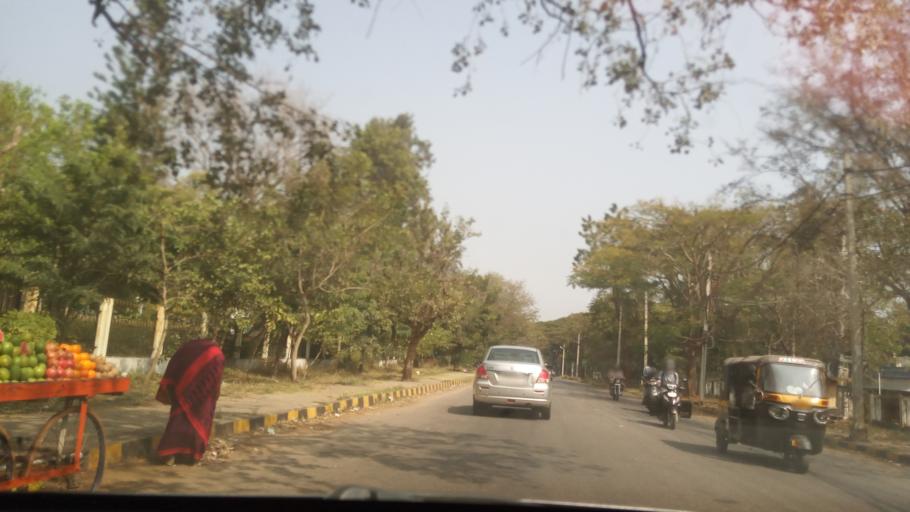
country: IN
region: Karnataka
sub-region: Mysore
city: Mysore
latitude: 12.3068
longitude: 76.6259
